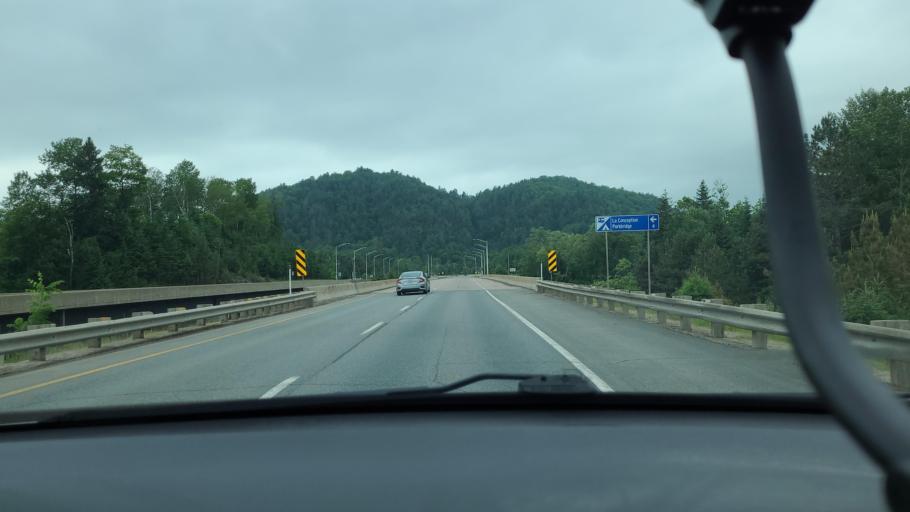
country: CA
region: Quebec
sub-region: Laurentides
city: Mont-Tremblant
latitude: 46.1572
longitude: -74.6948
